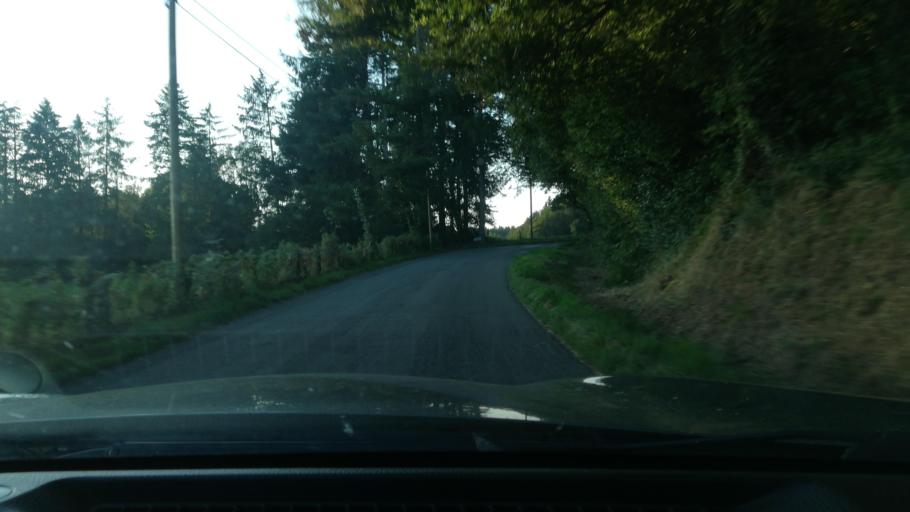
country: FR
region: Midi-Pyrenees
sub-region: Departement du Lot
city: Saint-Cere
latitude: 44.8842
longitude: 2.0282
